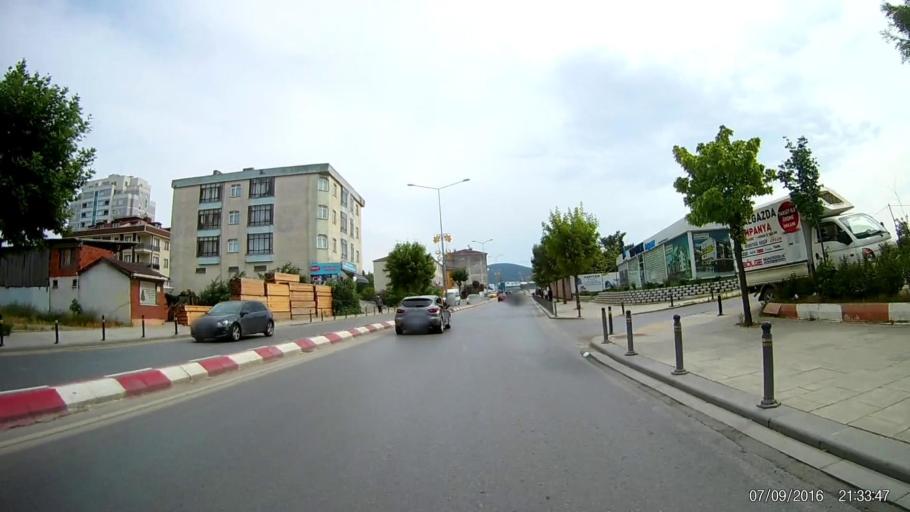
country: TR
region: Istanbul
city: Sultanbeyli
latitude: 40.9743
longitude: 29.2639
